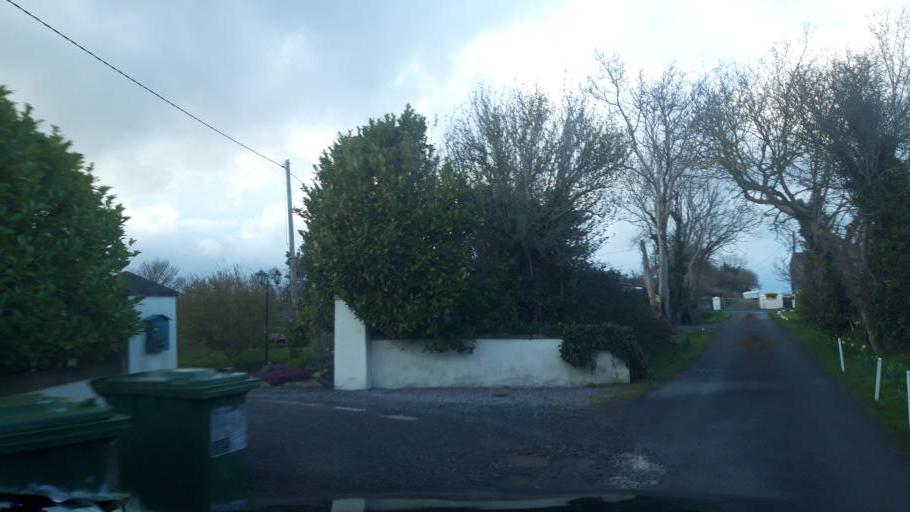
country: IE
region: Leinster
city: Portraine
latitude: 53.4940
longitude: -6.1234
